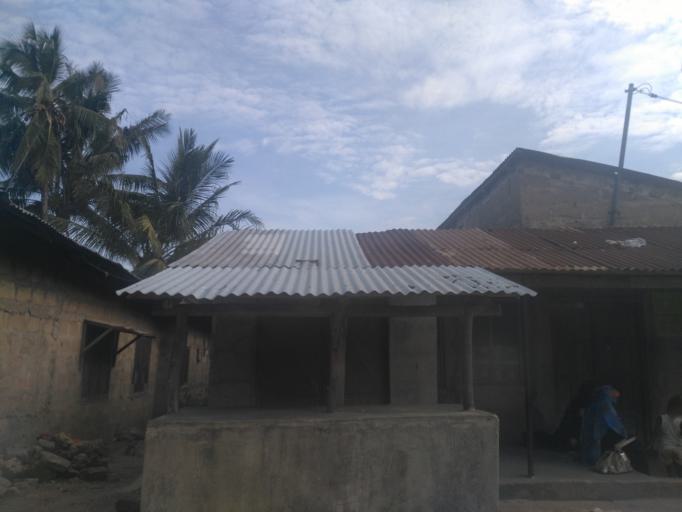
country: TZ
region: Zanzibar Urban/West
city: Zanzibar
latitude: -6.1527
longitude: 39.2107
